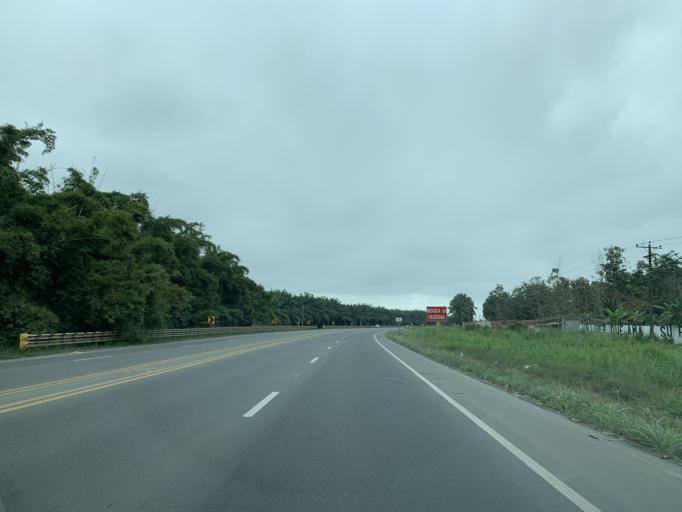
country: EC
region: Guayas
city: Coronel Marcelino Mariduena
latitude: -2.3255
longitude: -79.4488
